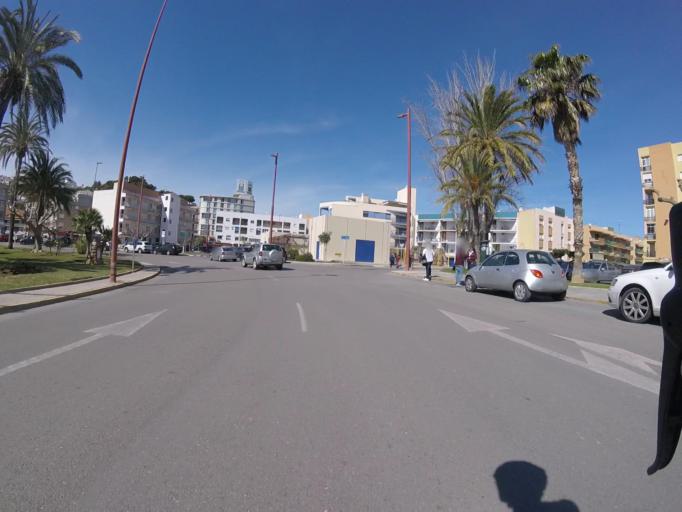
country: ES
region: Valencia
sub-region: Provincia de Castello
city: Peniscola
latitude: 40.3590
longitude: 0.3996
